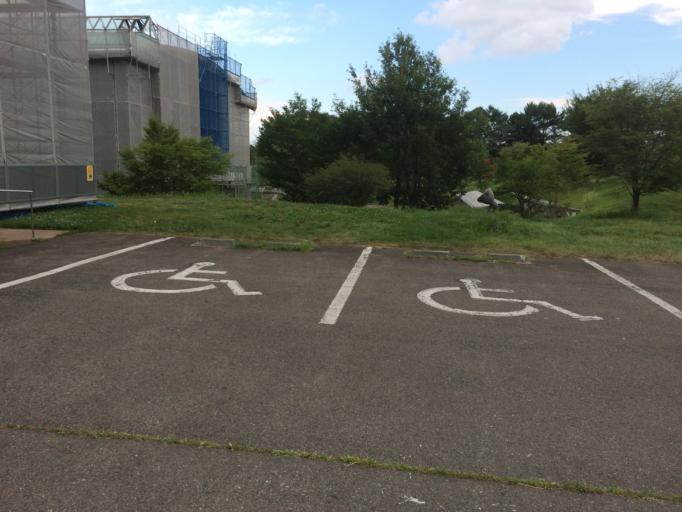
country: JP
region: Iwate
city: Morioka-shi
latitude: 39.8024
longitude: 141.1358
